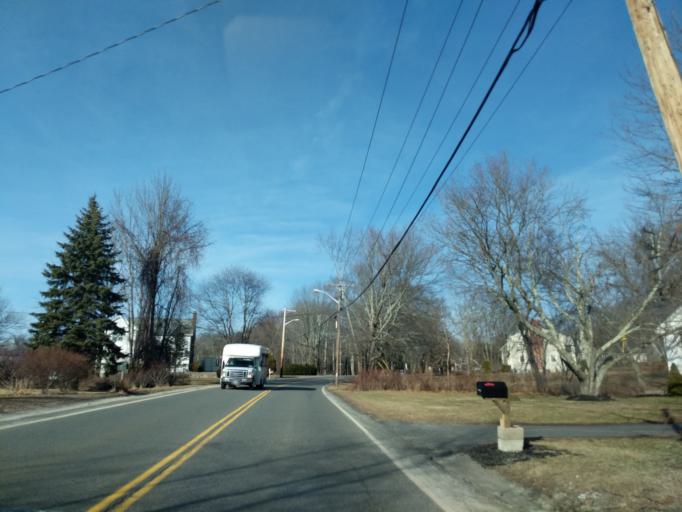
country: US
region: Massachusetts
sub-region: Worcester County
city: Blackstone
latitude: 42.0326
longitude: -71.5389
